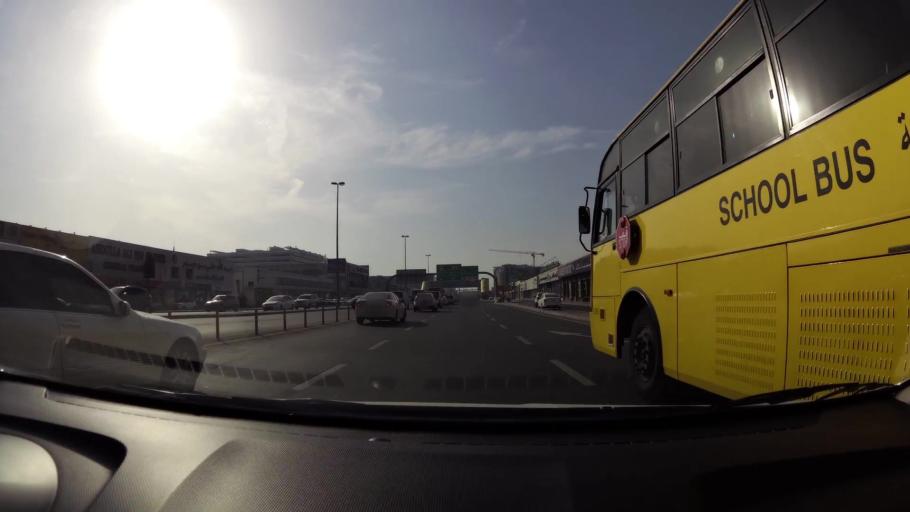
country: AE
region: Ash Shariqah
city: Sharjah
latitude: 25.2547
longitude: 55.3393
